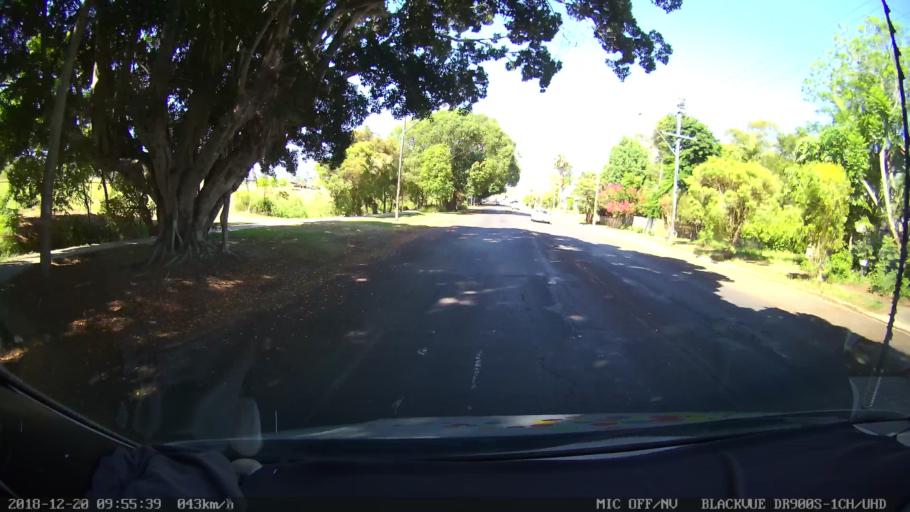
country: AU
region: New South Wales
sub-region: Lismore Municipality
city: Lismore
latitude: -28.8073
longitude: 153.2725
